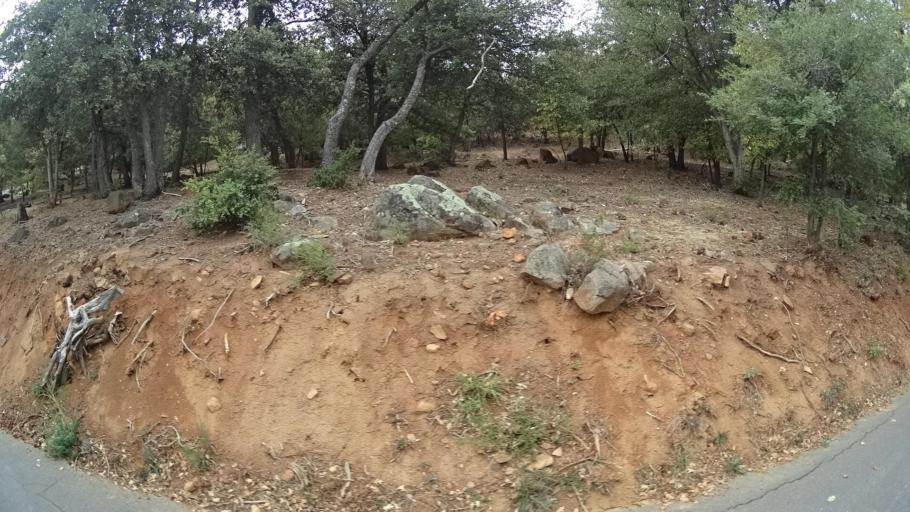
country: US
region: California
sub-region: San Diego County
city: Julian
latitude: 33.0514
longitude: -116.6279
